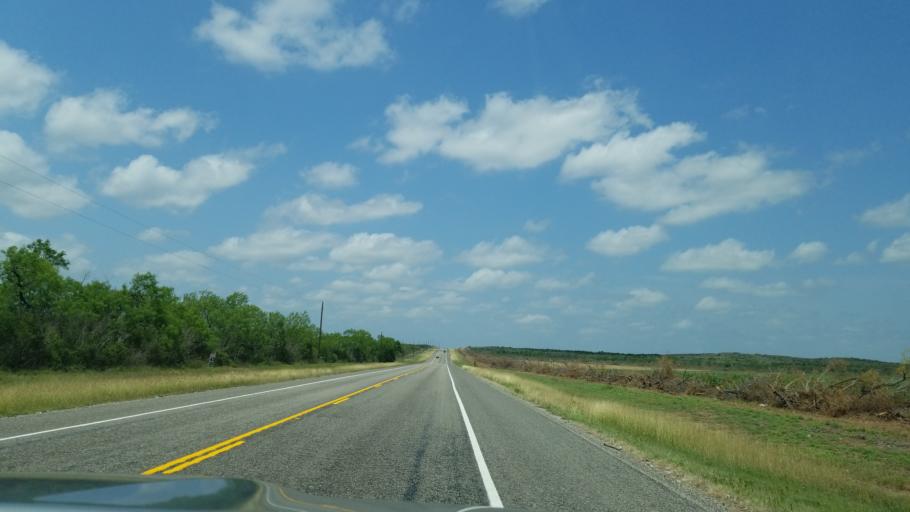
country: US
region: Texas
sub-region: Frio County
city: Pearsall
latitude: 28.9452
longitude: -99.2920
